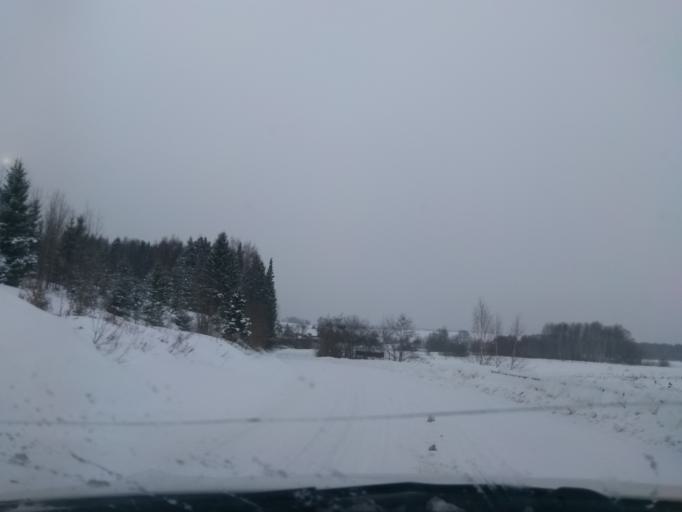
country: RU
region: Perm
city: Sylva
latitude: 57.8361
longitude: 56.7037
